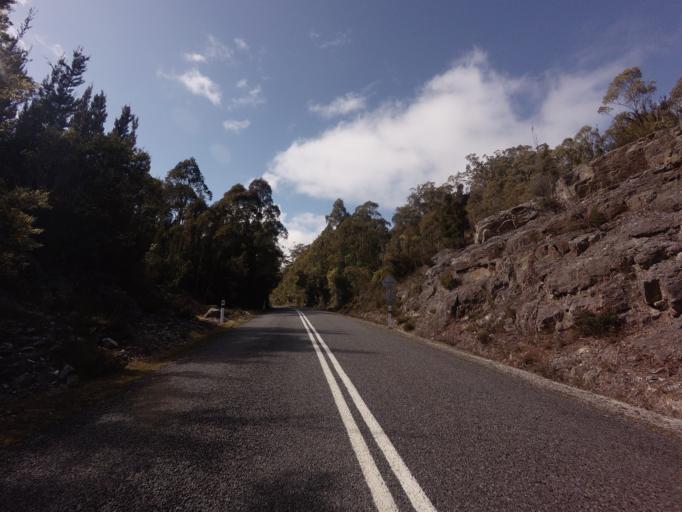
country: AU
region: Tasmania
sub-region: Huon Valley
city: Geeveston
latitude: -42.8138
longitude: 146.3790
